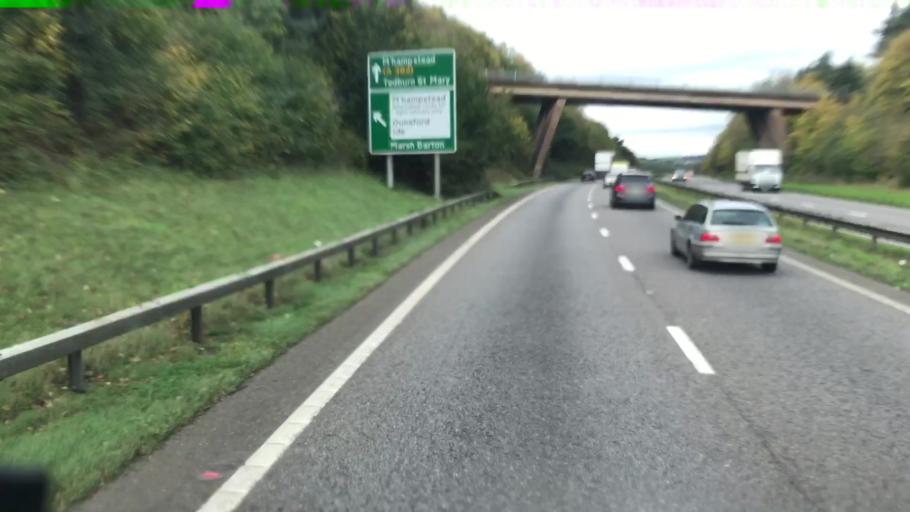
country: GB
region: England
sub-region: Devon
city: Exeter
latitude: 50.6921
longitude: -3.5386
